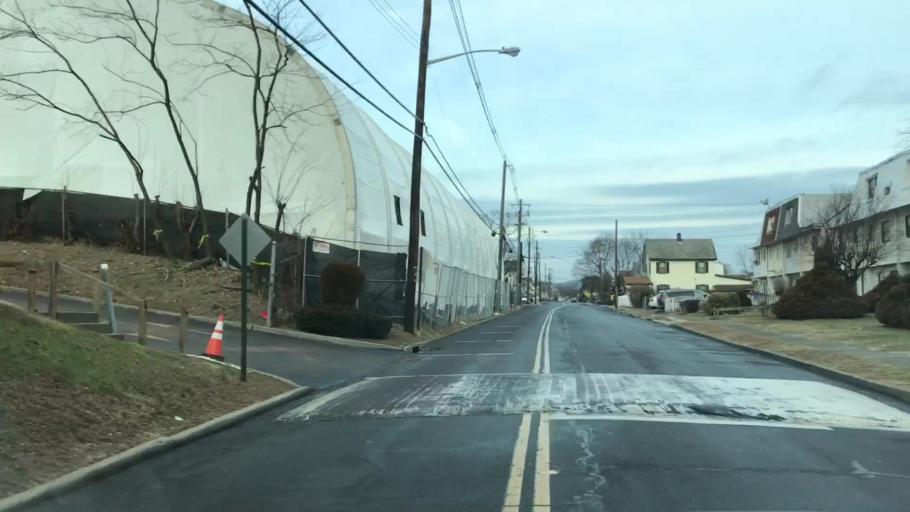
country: US
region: New York
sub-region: Rockland County
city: Haverstraw
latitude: 41.1926
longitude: -73.9618
